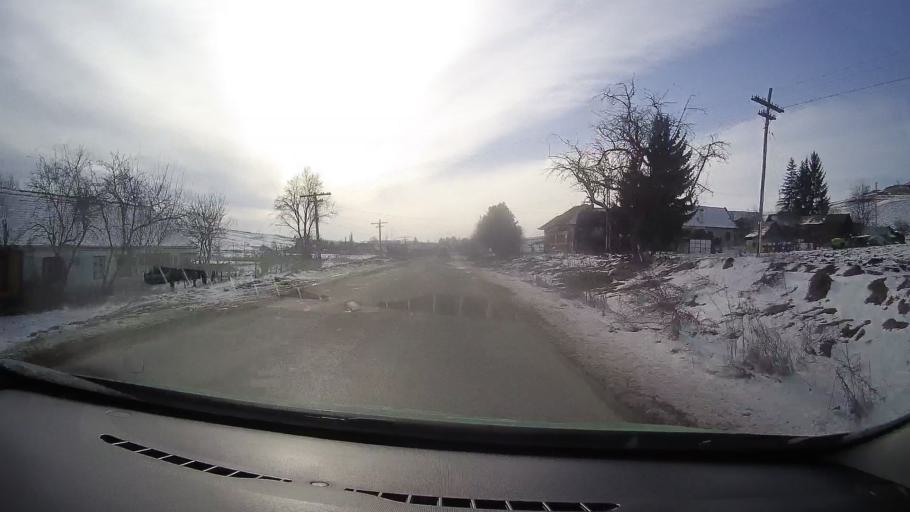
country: RO
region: Sibiu
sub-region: Oras Agnita
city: Ruja
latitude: 45.9869
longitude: 24.6513
